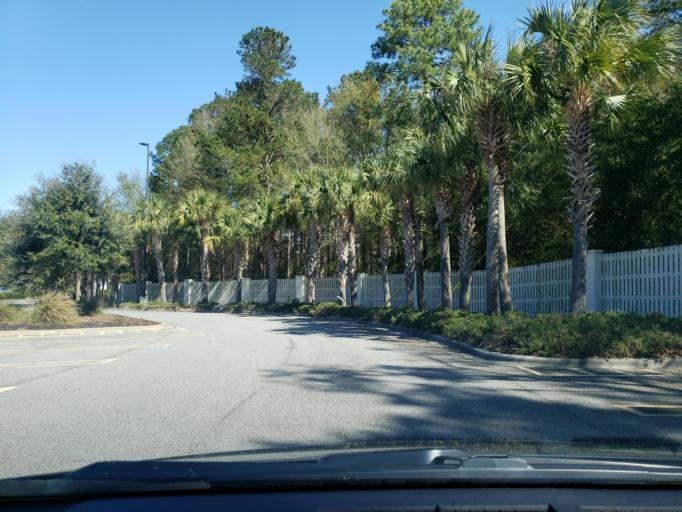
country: US
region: Georgia
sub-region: Chatham County
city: Isle of Hope
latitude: 31.9873
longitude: -81.0798
